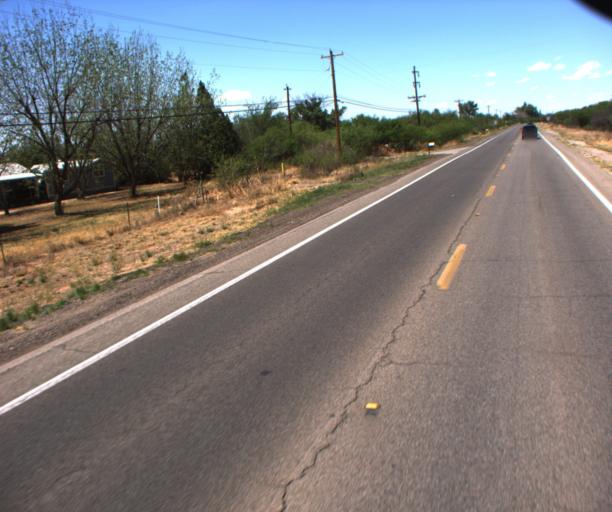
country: US
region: Arizona
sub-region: Cochise County
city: Saint David
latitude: 31.8774
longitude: -110.2111
